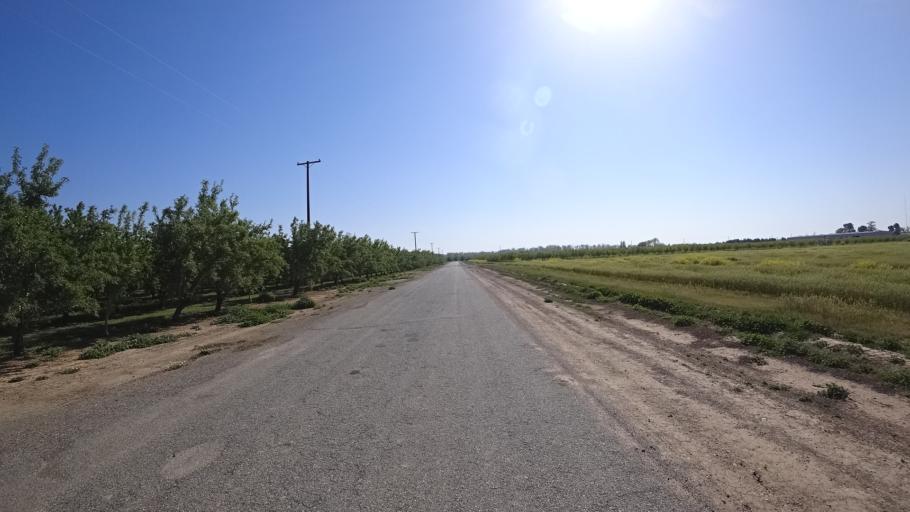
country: US
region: California
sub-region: Glenn County
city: Hamilton City
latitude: 39.6378
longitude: -122.0118
